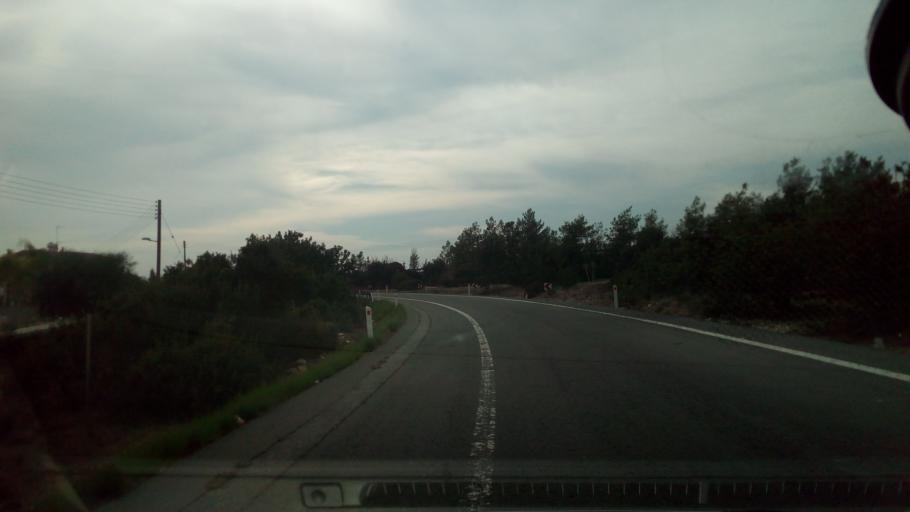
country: CY
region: Larnaka
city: Tersefanou
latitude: 34.8700
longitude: 33.4956
